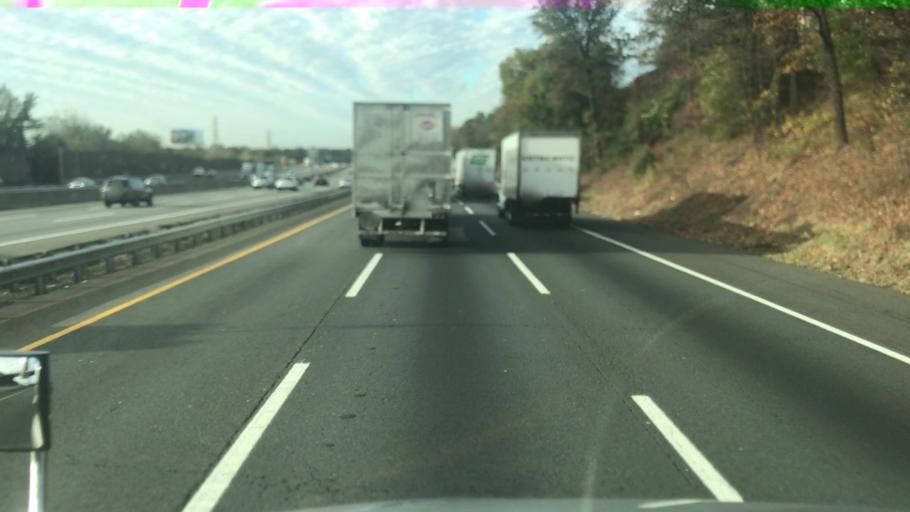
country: US
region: New Jersey
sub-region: Middlesex County
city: Fords
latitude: 40.5348
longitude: -74.3279
